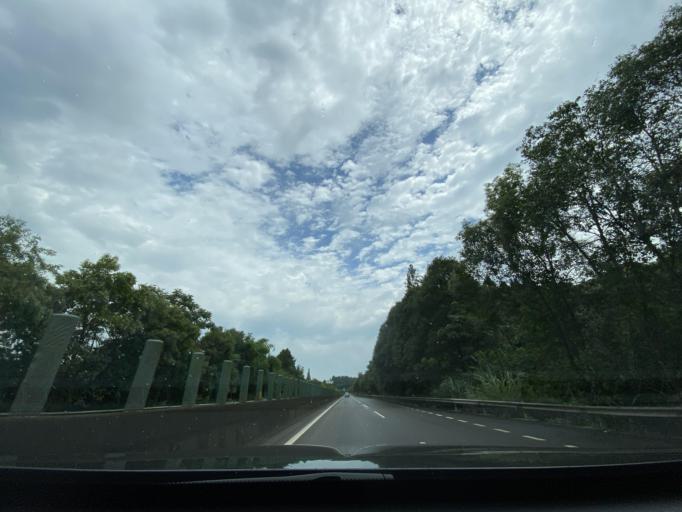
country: CN
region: Sichuan
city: Jiancheng
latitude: 30.3021
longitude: 104.5793
